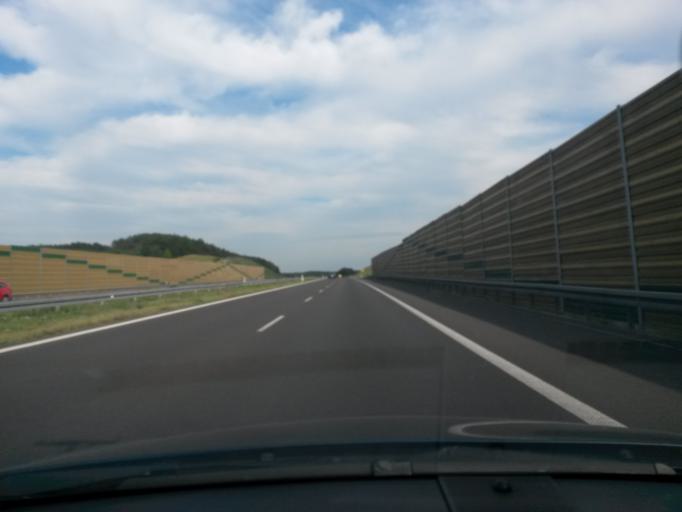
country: PL
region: Greater Poland Voivodeship
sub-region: Powiat turecki
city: Wladyslawow
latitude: 52.1443
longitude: 18.5159
